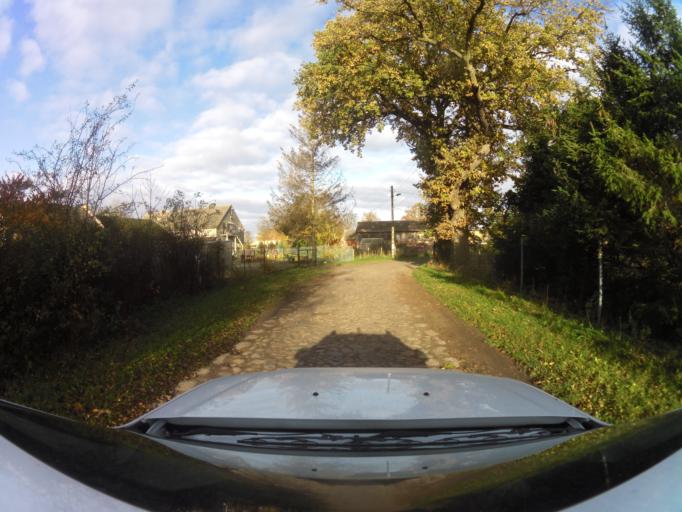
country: PL
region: West Pomeranian Voivodeship
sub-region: Powiat gryficki
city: Cerkwica
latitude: 54.0608
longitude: 15.1728
